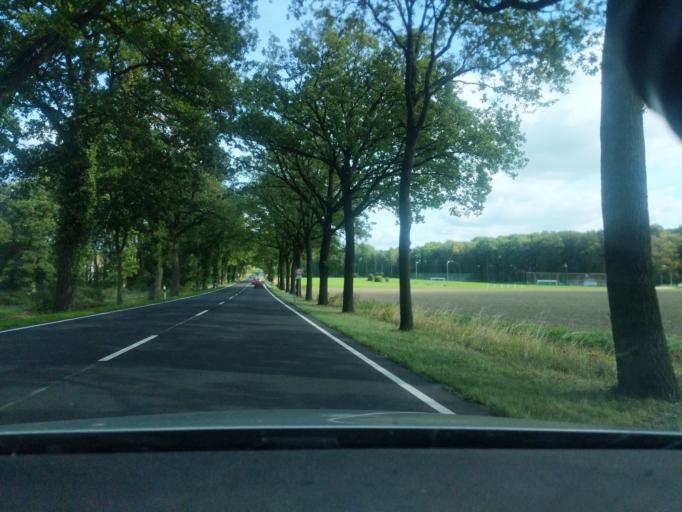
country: DE
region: Lower Saxony
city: Belm
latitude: 52.3331
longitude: 8.1756
